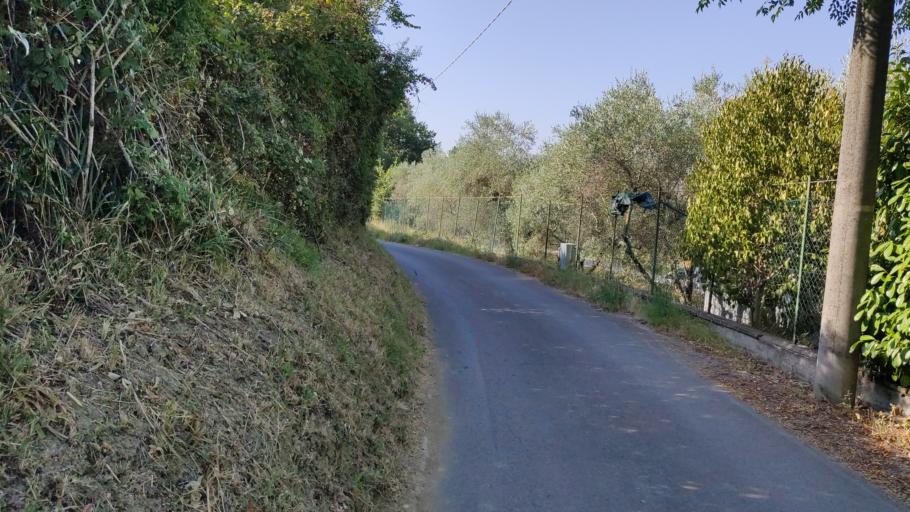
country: IT
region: Umbria
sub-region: Provincia di Terni
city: Amelia
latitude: 42.5356
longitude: 12.4105
